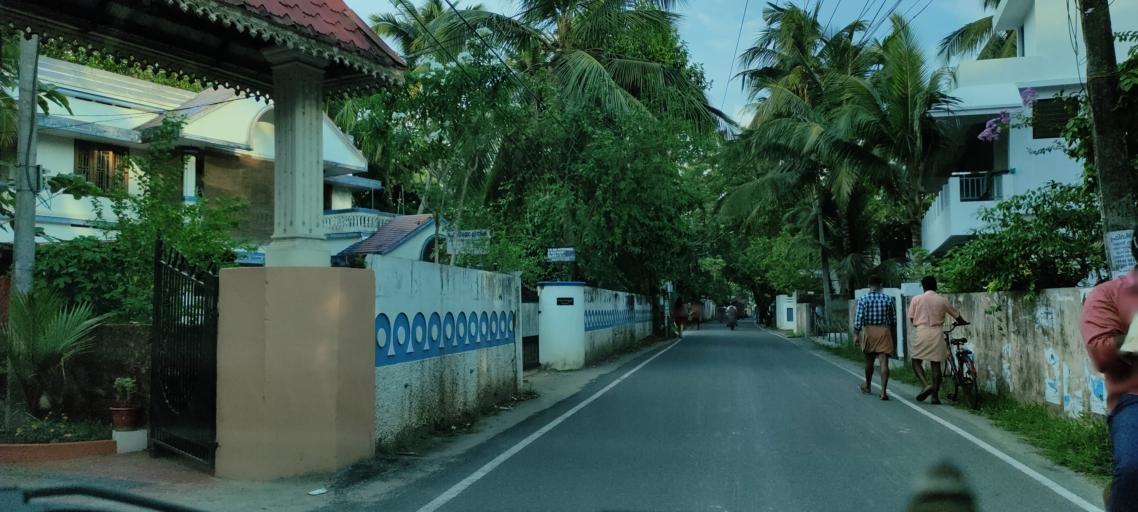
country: IN
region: Kerala
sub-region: Alappuzha
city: Arukutti
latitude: 9.8938
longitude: 76.3106
